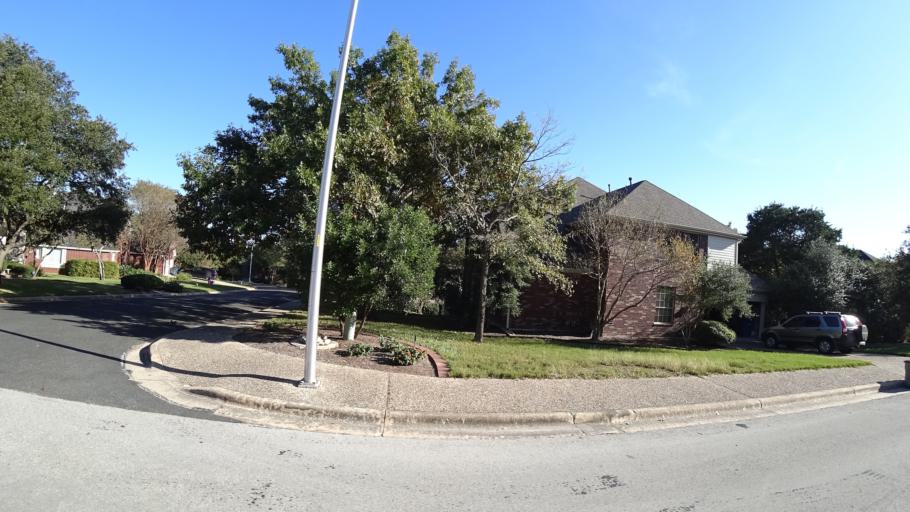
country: US
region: Texas
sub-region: Williamson County
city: Jollyville
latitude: 30.4180
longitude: -97.7778
